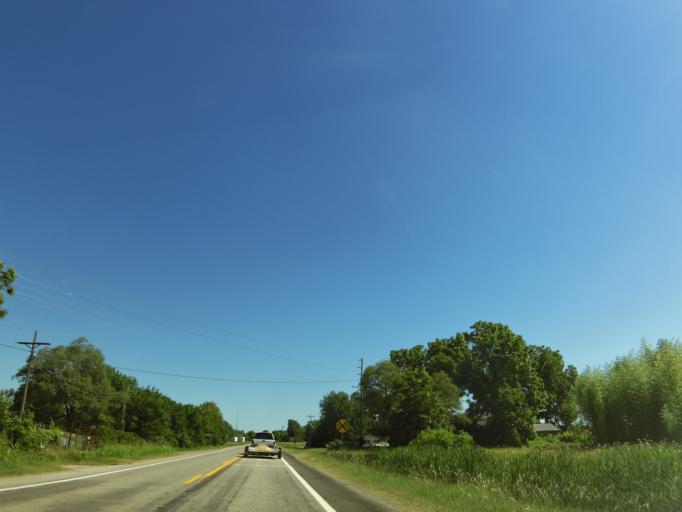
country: US
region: Arkansas
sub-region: Clay County
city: Piggott
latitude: 36.4437
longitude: -90.1472
